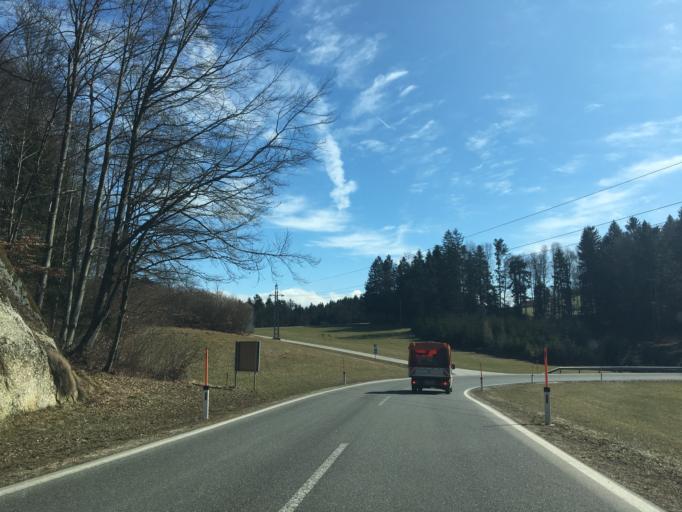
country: AT
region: Upper Austria
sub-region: Politischer Bezirk Perg
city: Sankt Georgen am Walde
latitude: 48.3024
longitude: 14.9063
